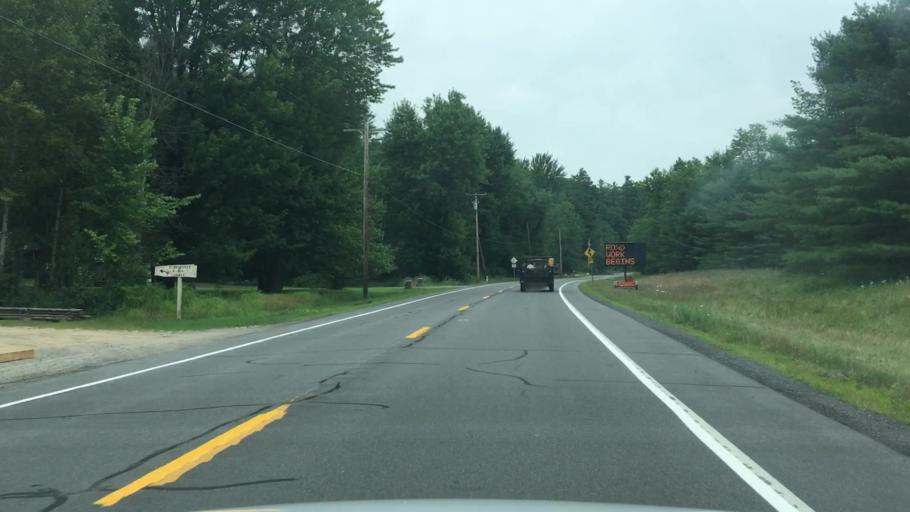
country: US
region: New York
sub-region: Clinton County
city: Peru
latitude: 44.4466
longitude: -73.6580
